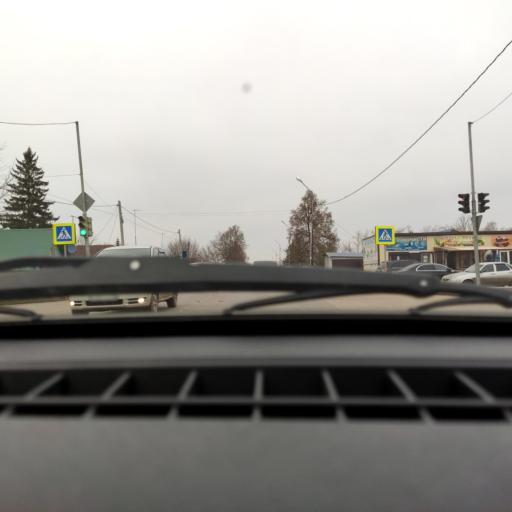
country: RU
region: Bashkortostan
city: Chishmy
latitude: 54.5901
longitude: 55.3933
